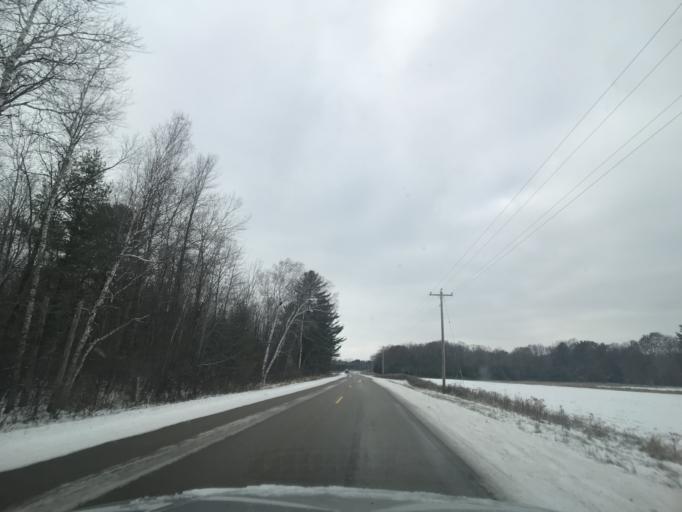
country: US
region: Wisconsin
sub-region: Brown County
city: Suamico
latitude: 44.7063
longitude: -88.0739
